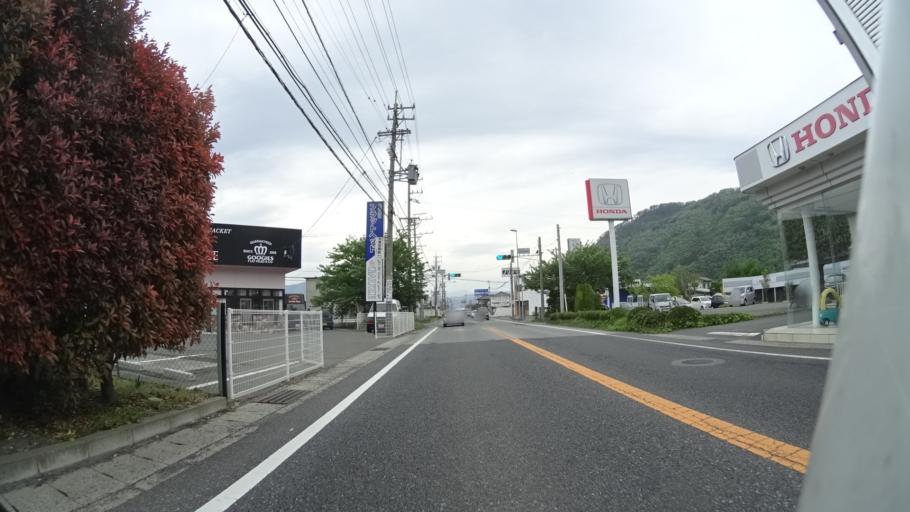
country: JP
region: Nagano
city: Nagano-shi
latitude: 36.5059
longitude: 138.1414
